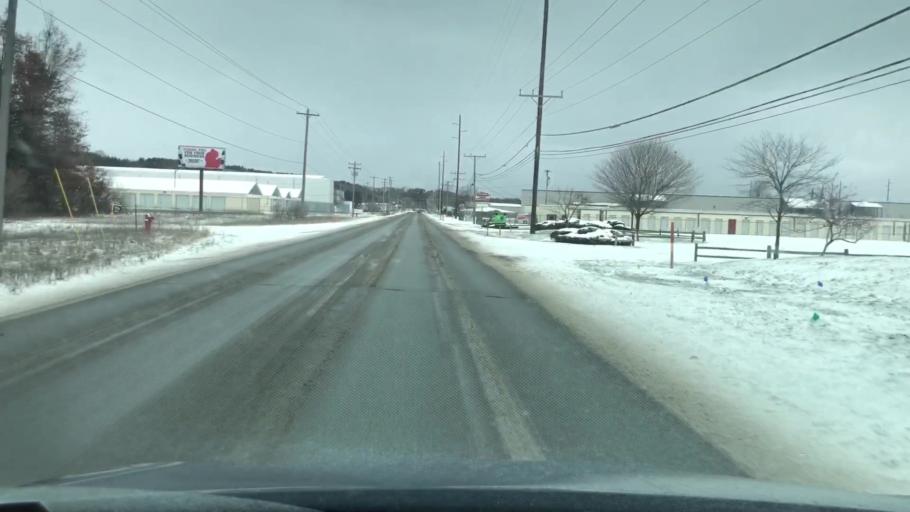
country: US
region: Michigan
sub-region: Grand Traverse County
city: Traverse City
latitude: 44.7232
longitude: -85.6258
